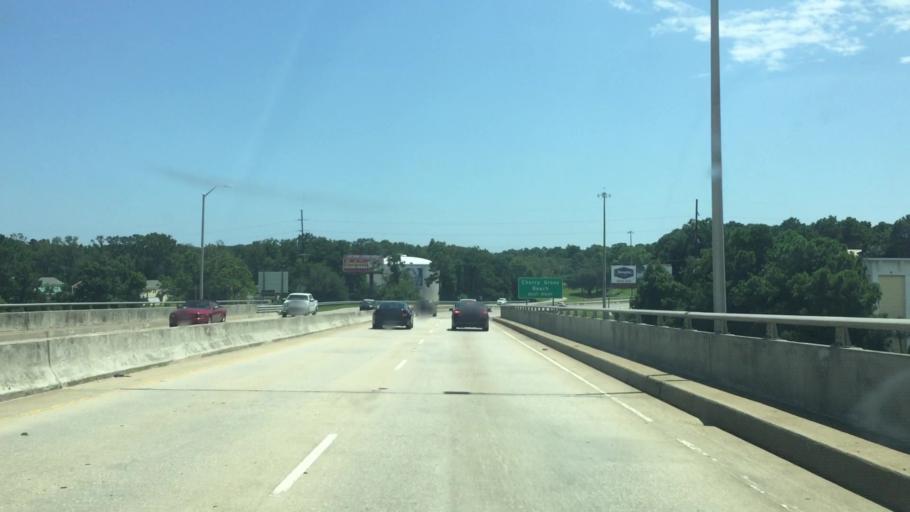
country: US
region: South Carolina
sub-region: Horry County
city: North Myrtle Beach
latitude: 33.8512
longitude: -78.6534
